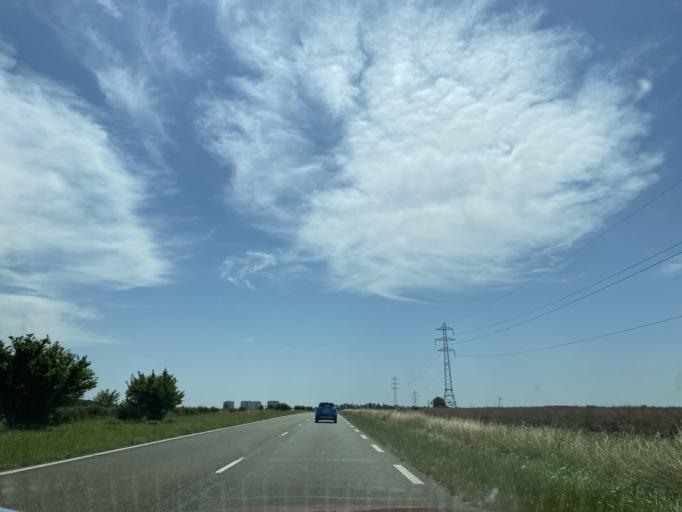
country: FR
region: Centre
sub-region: Departement d'Eure-et-Loir
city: Mainvilliers
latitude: 48.4634
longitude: 1.4632
